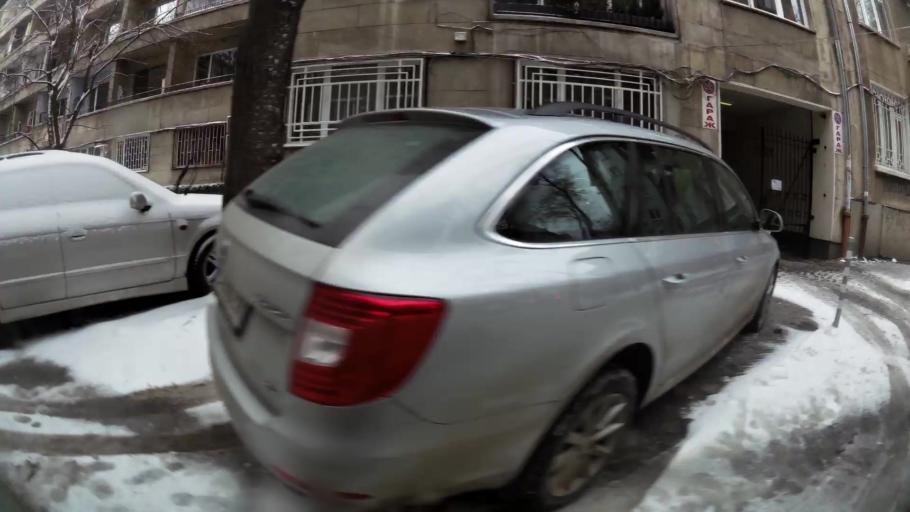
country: BG
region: Sofia-Capital
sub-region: Stolichna Obshtina
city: Sofia
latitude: 42.6931
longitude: 23.3392
